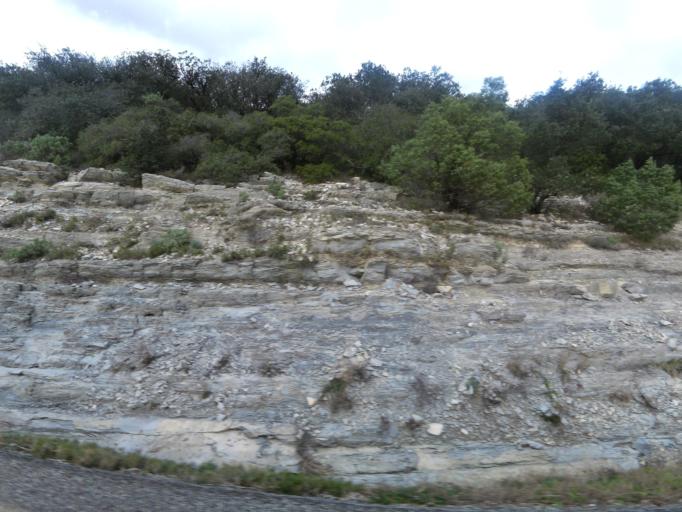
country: FR
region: Languedoc-Roussillon
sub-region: Departement du Gard
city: Clarensac
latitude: 43.8348
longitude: 4.1901
